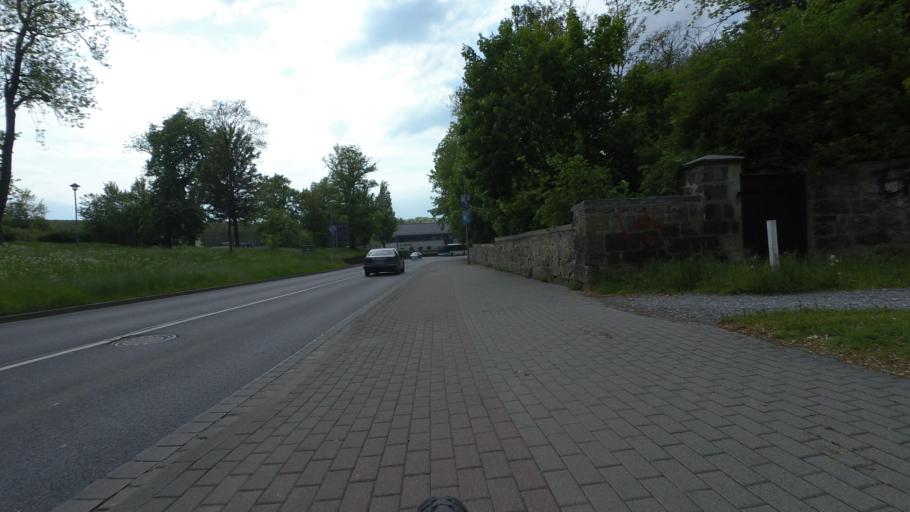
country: DE
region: Saxony-Anhalt
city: Halberstadt
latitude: 51.8936
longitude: 11.0381
